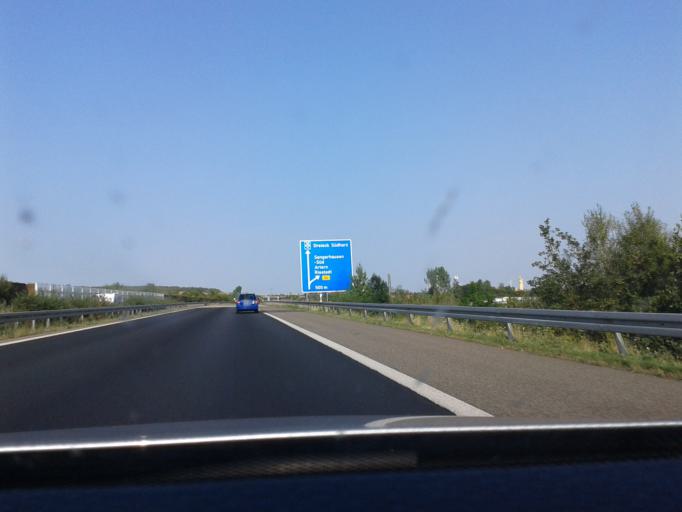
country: DE
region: Saxony-Anhalt
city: Sangerhausen
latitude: 51.4507
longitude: 11.2899
